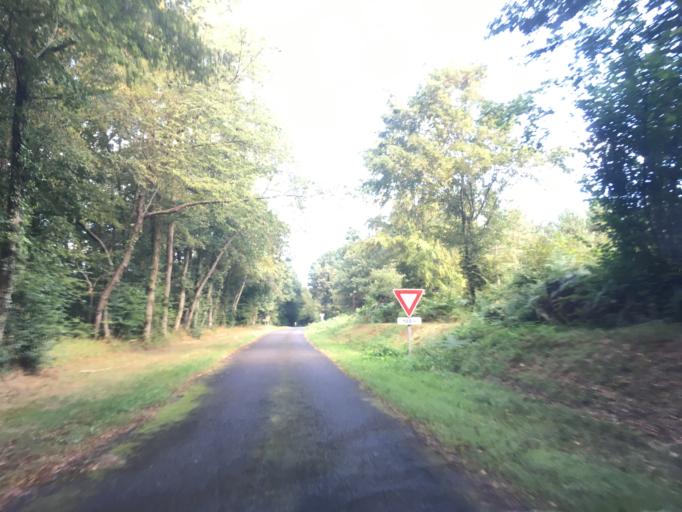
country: FR
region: Haute-Normandie
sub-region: Departement de l'Eure
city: Courcelles-sur-Seine
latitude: 49.1791
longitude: 1.3886
